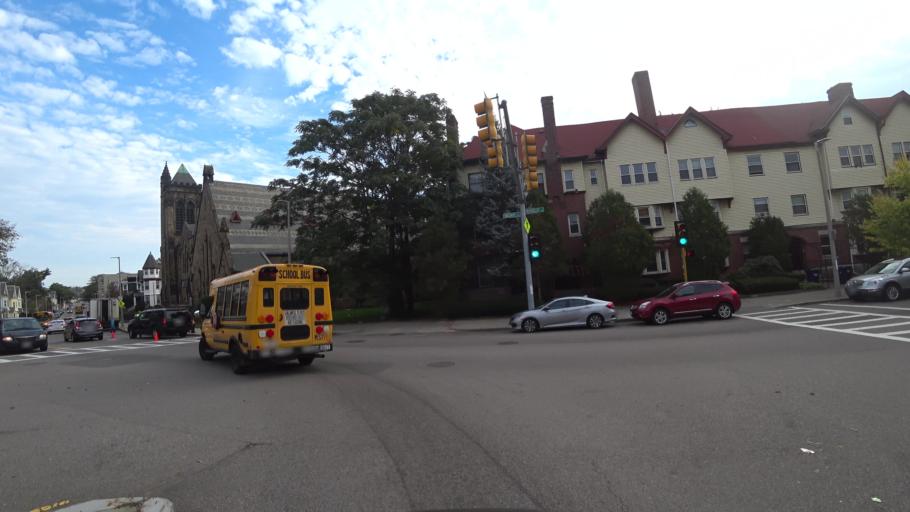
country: US
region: Massachusetts
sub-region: Suffolk County
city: Jamaica Plain
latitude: 42.3206
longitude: -71.0861
